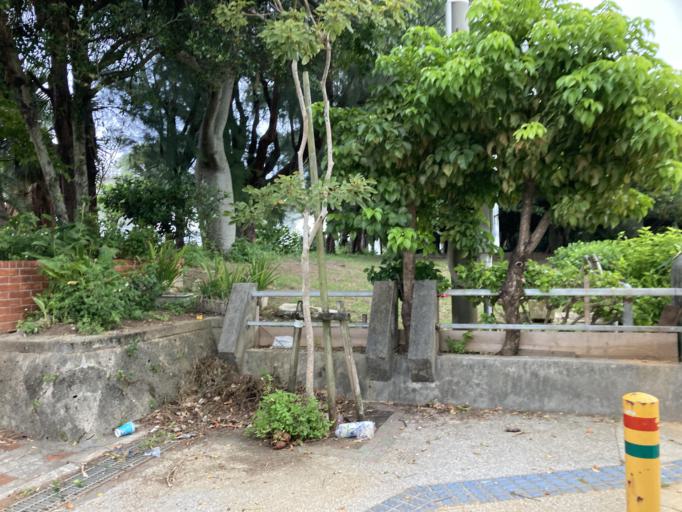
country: JP
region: Okinawa
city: Naha-shi
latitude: 26.2236
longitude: 127.6765
